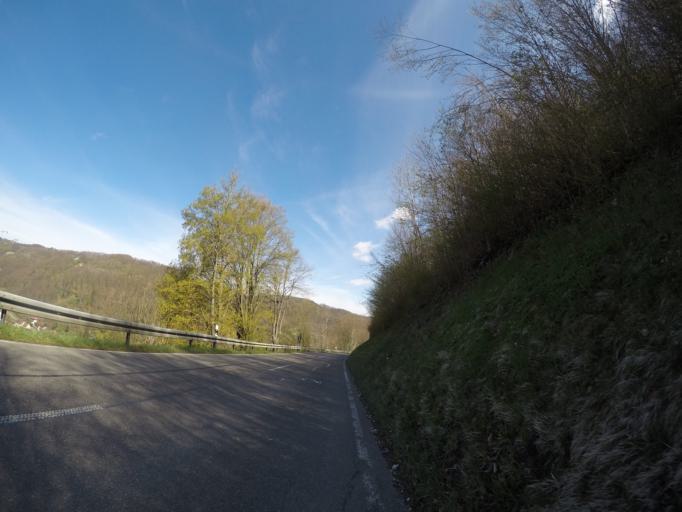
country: DE
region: Baden-Wuerttemberg
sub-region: Regierungsbezirk Stuttgart
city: Wiesensteig
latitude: 48.5594
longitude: 9.6295
